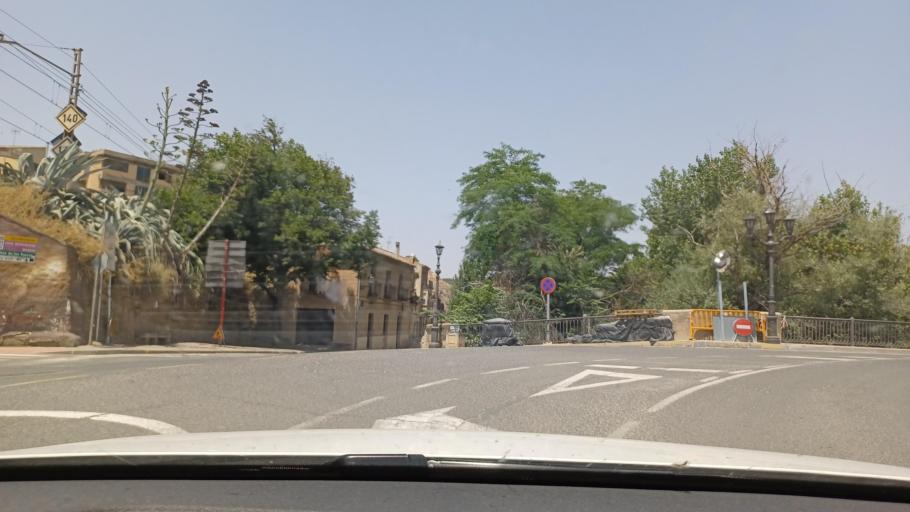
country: ES
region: Navarre
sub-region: Provincia de Navarra
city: Tudela
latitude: 42.0652
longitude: -1.6033
